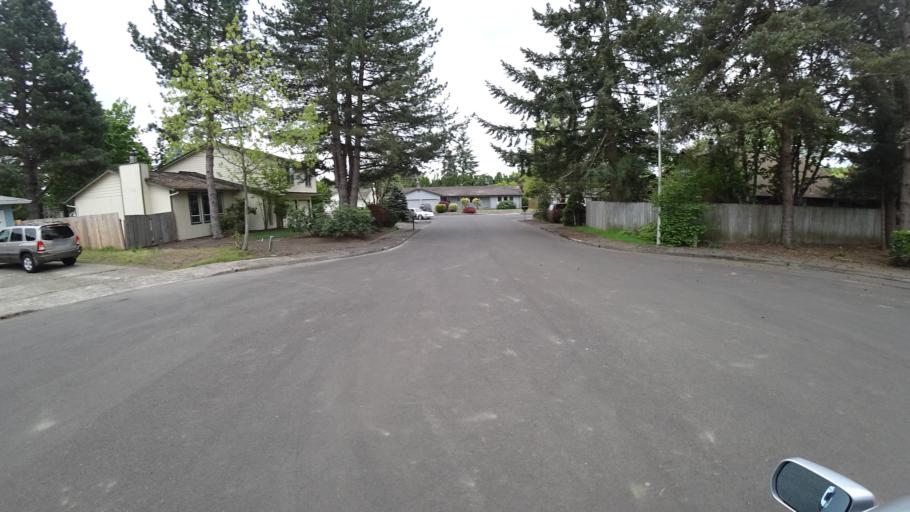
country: US
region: Oregon
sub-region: Washington County
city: Hillsboro
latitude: 45.5355
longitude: -122.9750
